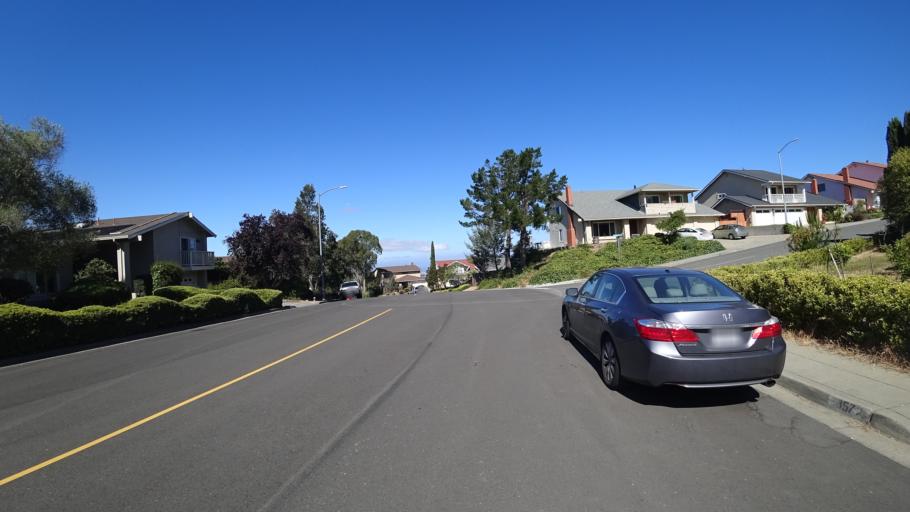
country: US
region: California
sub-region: Alameda County
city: Fairview
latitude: 37.6507
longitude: -122.0281
